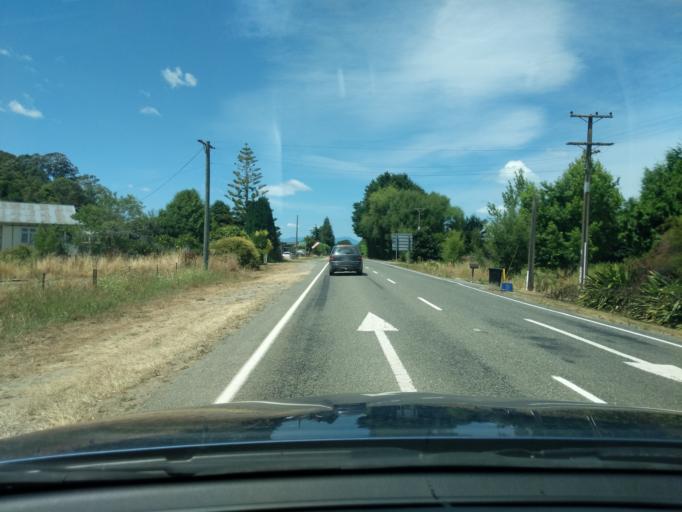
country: NZ
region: Tasman
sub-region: Tasman District
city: Motueka
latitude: -41.0588
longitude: 172.9698
